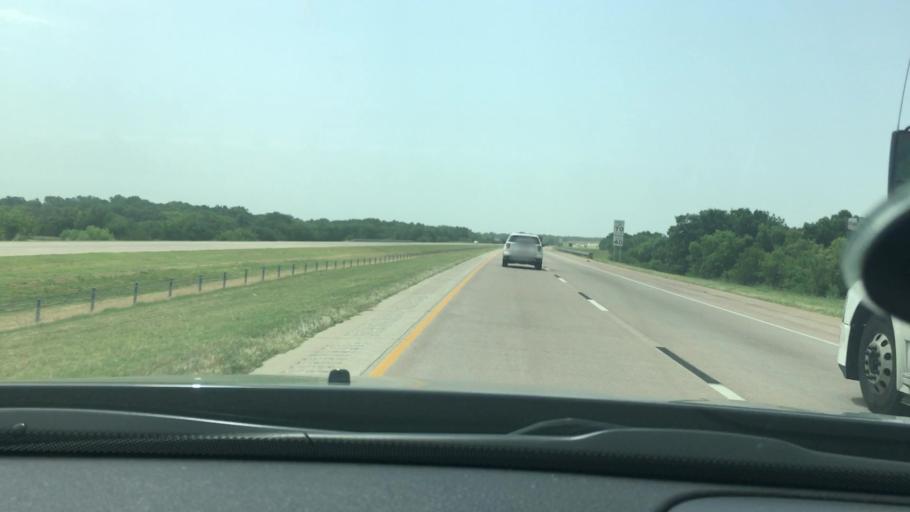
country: US
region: Oklahoma
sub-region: Garvin County
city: Pauls Valley
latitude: 34.6982
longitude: -97.2383
